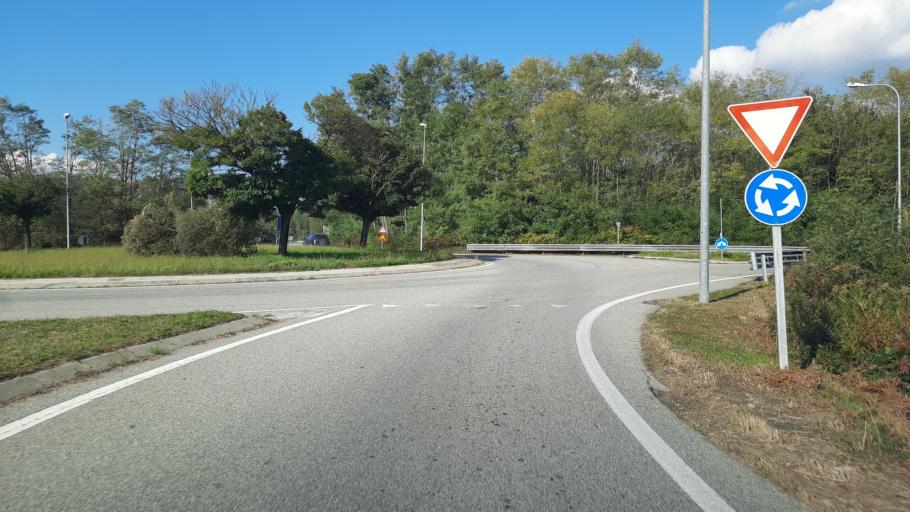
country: IT
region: Piedmont
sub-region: Provincia di Novara
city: Gargallo
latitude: 45.7277
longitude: 8.4368
